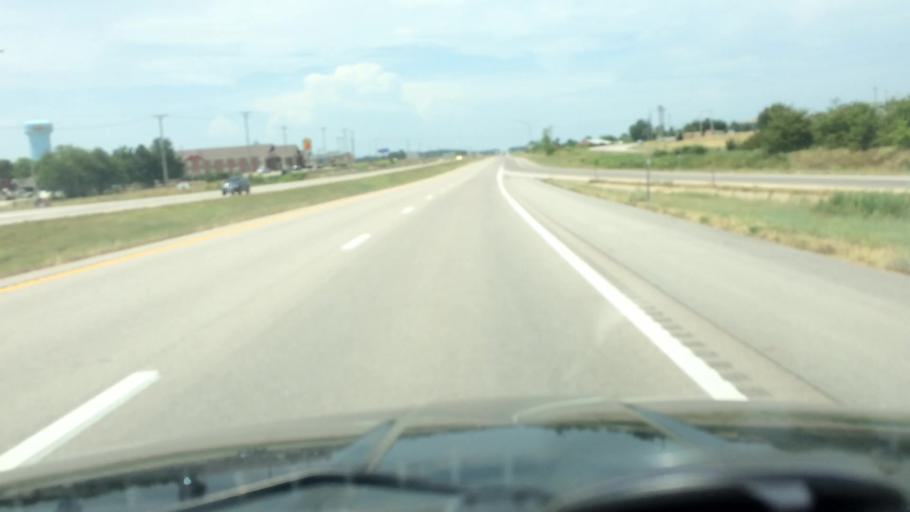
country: US
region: Missouri
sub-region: Polk County
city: Bolivar
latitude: 37.5949
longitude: -93.4340
